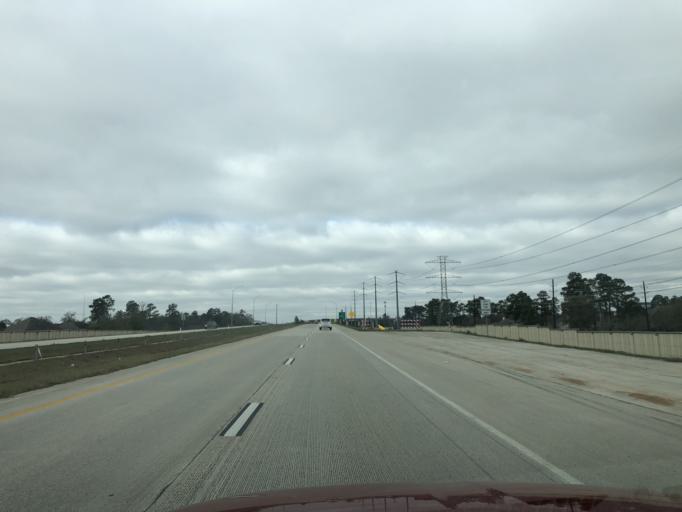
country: US
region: Texas
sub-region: Harris County
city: Spring
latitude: 30.0928
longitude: -95.4248
